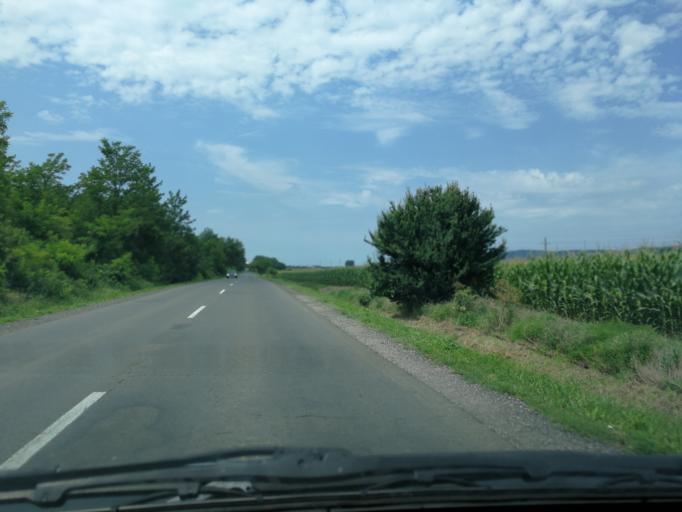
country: HU
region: Baranya
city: Siklos
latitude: 45.8501
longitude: 18.3435
